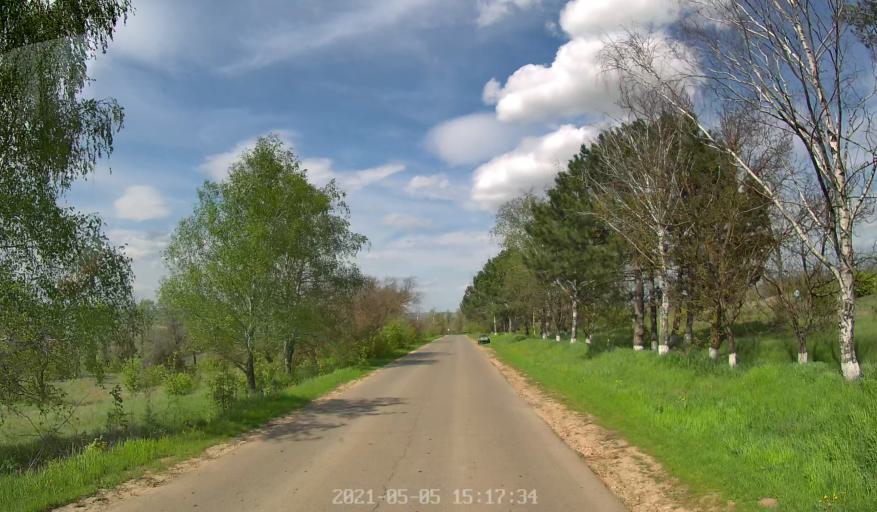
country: MD
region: Criuleni
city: Criuleni
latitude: 47.1129
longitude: 29.1941
